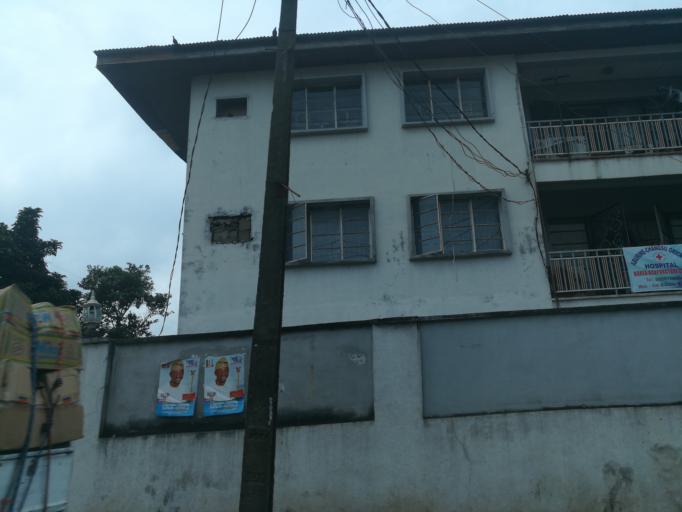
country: NG
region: Lagos
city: Ojota
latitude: 6.5689
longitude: 3.3645
